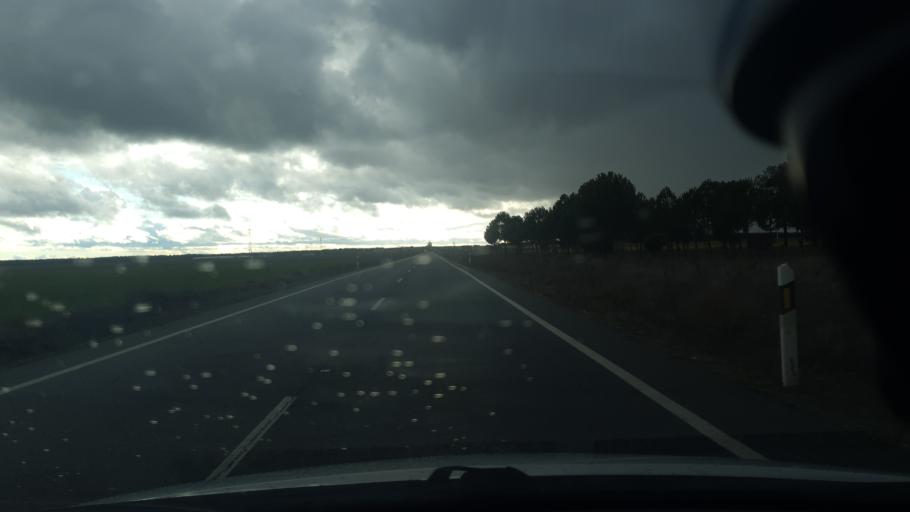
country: ES
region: Castille and Leon
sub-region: Provincia de Segovia
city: Chane
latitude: 41.3104
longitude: -4.3953
